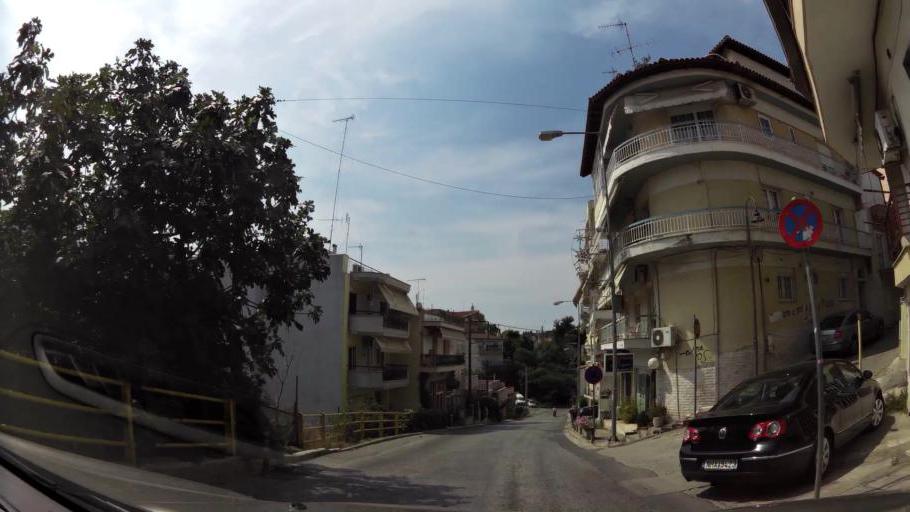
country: GR
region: Central Macedonia
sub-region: Nomos Thessalonikis
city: Sykies
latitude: 40.6457
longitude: 22.9547
